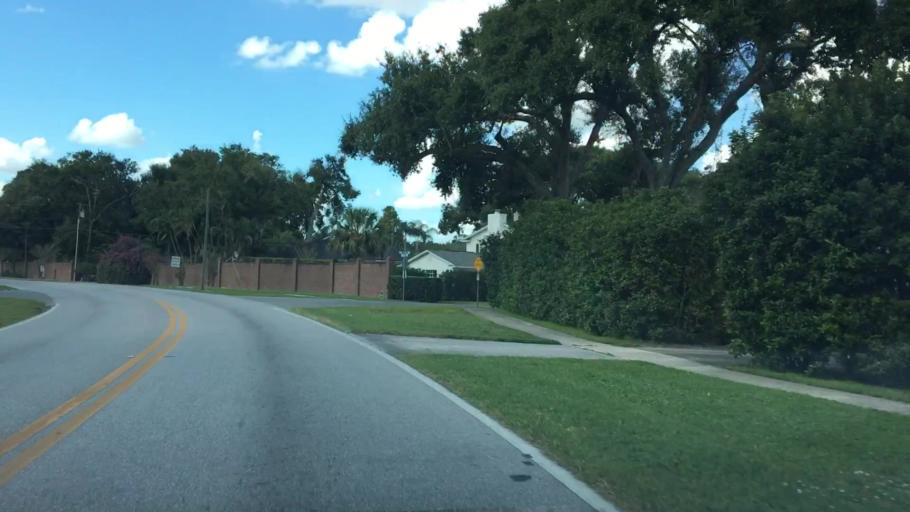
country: US
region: Florida
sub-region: Orange County
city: Pine Castle
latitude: 28.4839
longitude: -81.3479
